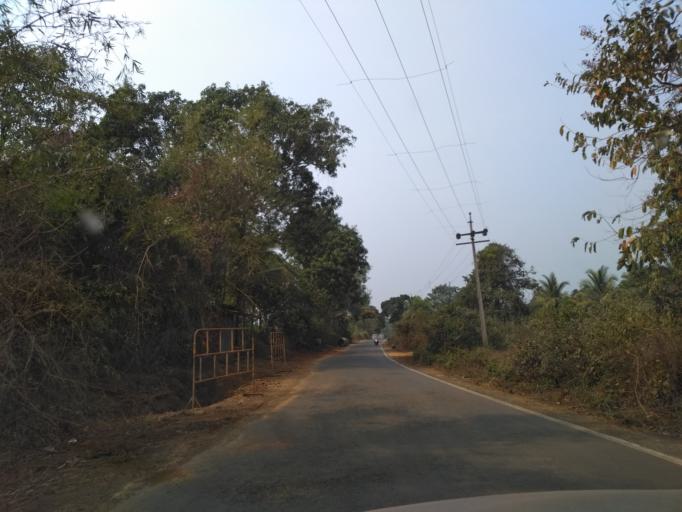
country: IN
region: Goa
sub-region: North Goa
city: Dicholi
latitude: 15.7306
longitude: 73.9507
